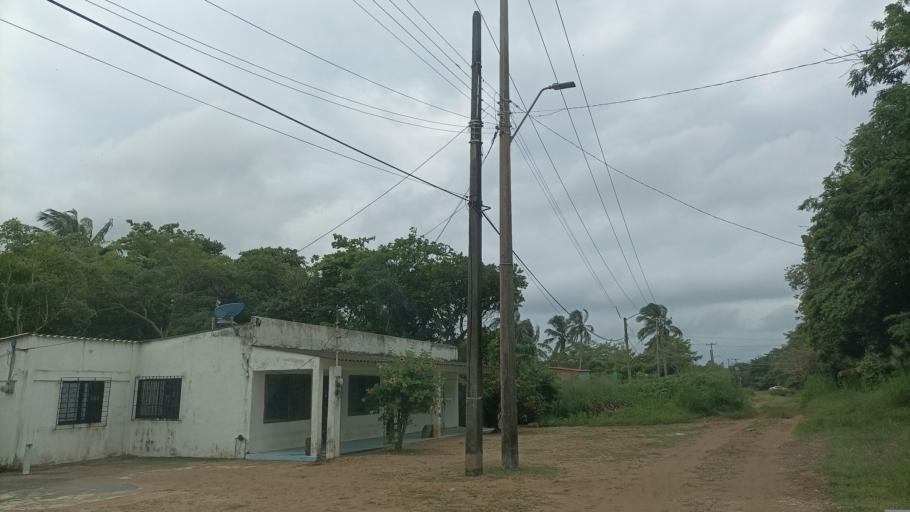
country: MX
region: Veracruz
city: Agua Dulce
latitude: 18.2073
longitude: -94.1392
